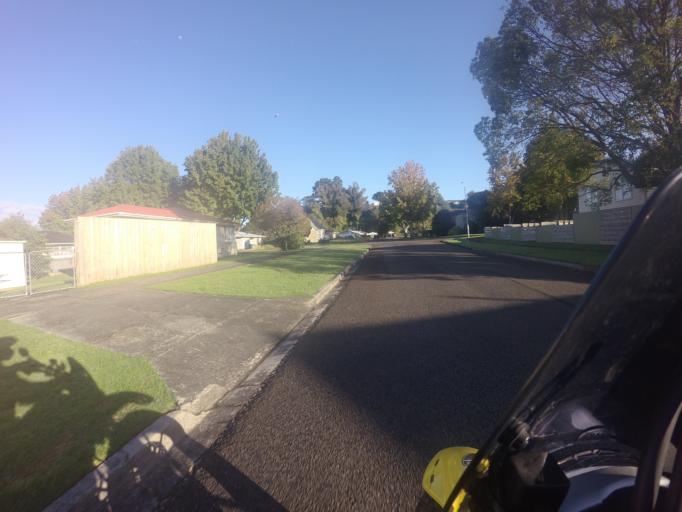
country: NZ
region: Gisborne
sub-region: Gisborne District
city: Gisborne
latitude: -38.6679
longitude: 178.0562
